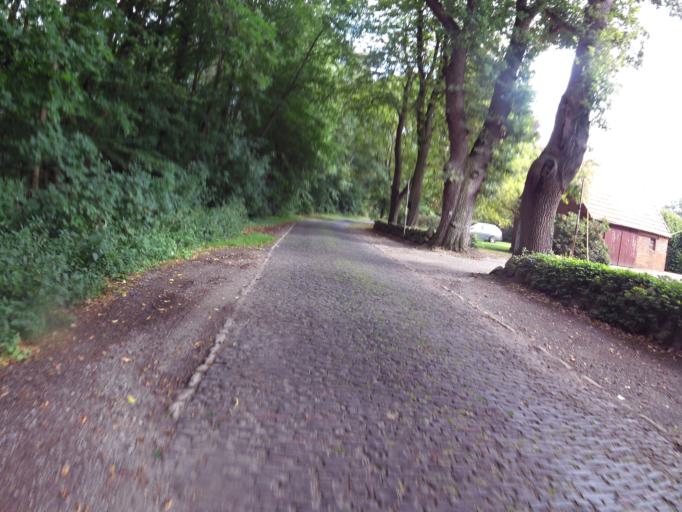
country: DE
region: Lower Saxony
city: Kohlen
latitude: 53.5052
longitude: 8.9111
